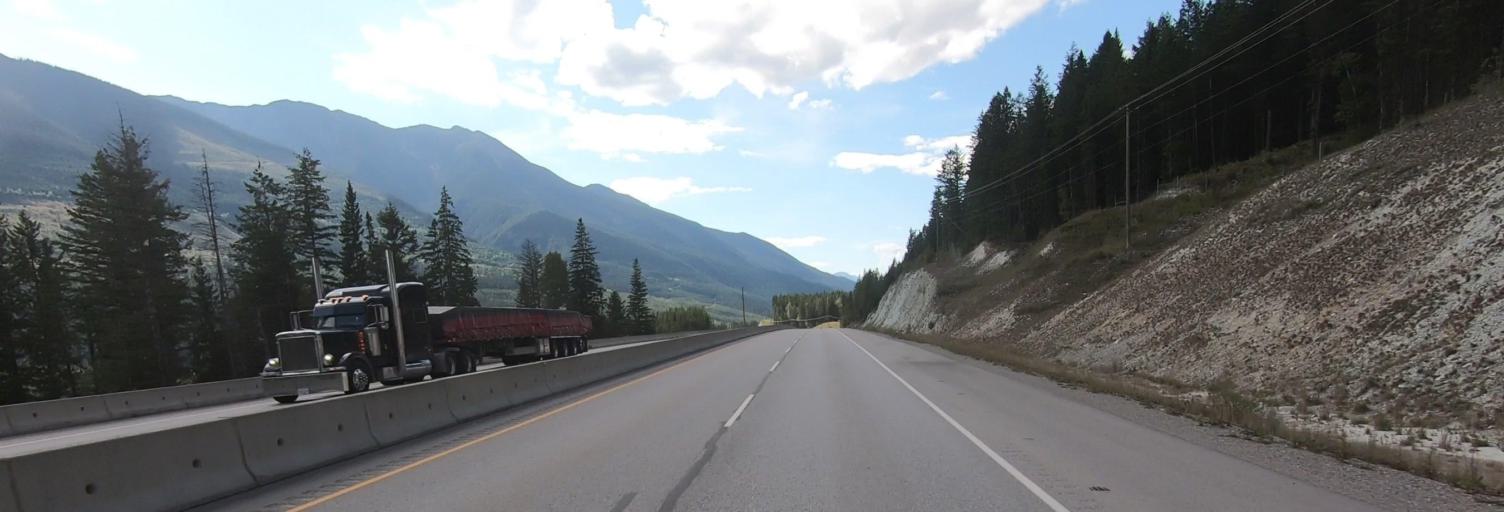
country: CA
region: British Columbia
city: Golden
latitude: 51.2595
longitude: -116.7160
